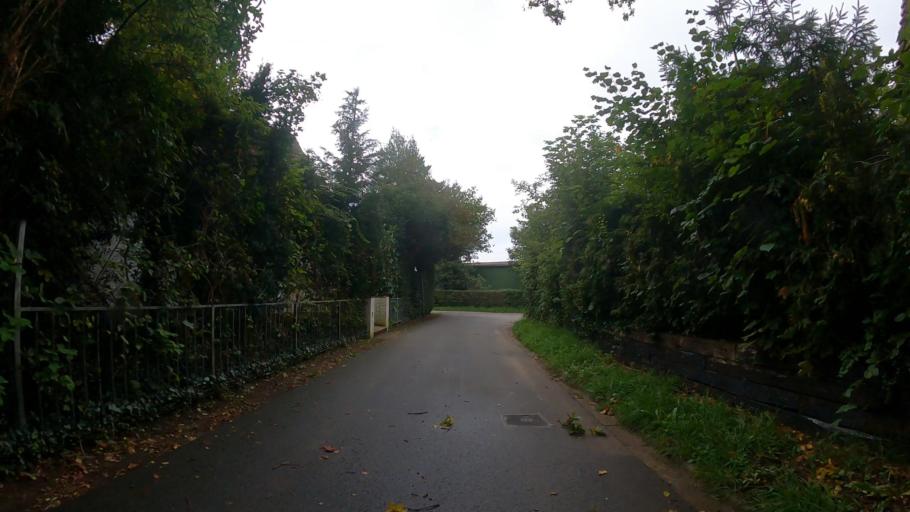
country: DE
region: Schleswig-Holstein
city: Prisdorf
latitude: 53.6759
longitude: 9.7567
